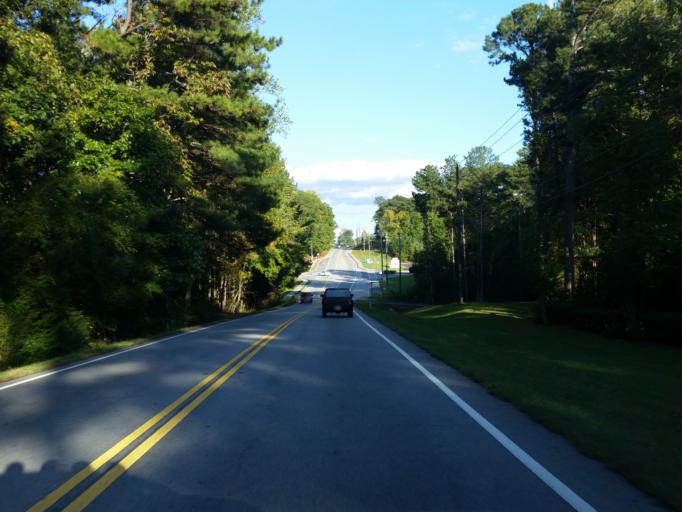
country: US
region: Georgia
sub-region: Cobb County
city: Powder Springs
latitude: 33.9029
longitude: -84.6938
